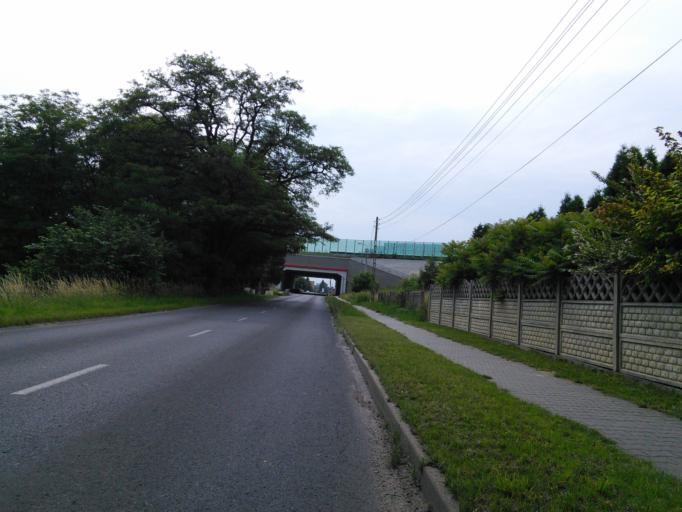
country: PL
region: Silesian Voivodeship
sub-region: Powiat bedzinski
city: Bobrowniki
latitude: 50.3754
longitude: 18.9684
